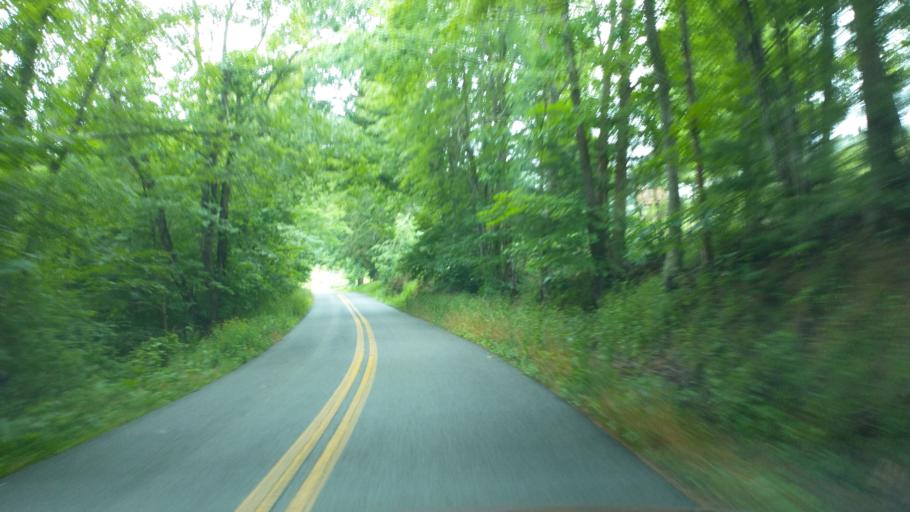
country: US
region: West Virginia
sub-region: Mercer County
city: Athens
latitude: 37.4355
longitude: -80.9703
